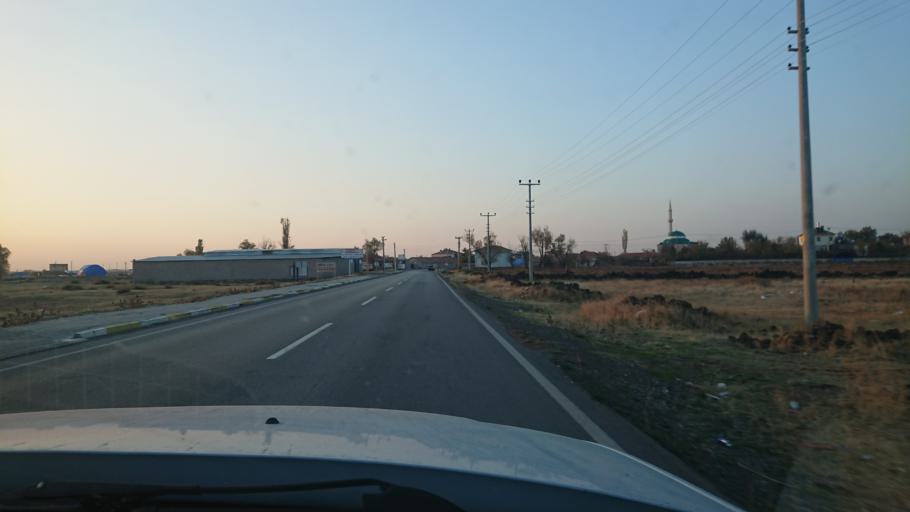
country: TR
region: Aksaray
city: Aksaray
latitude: 38.3162
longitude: 34.0551
